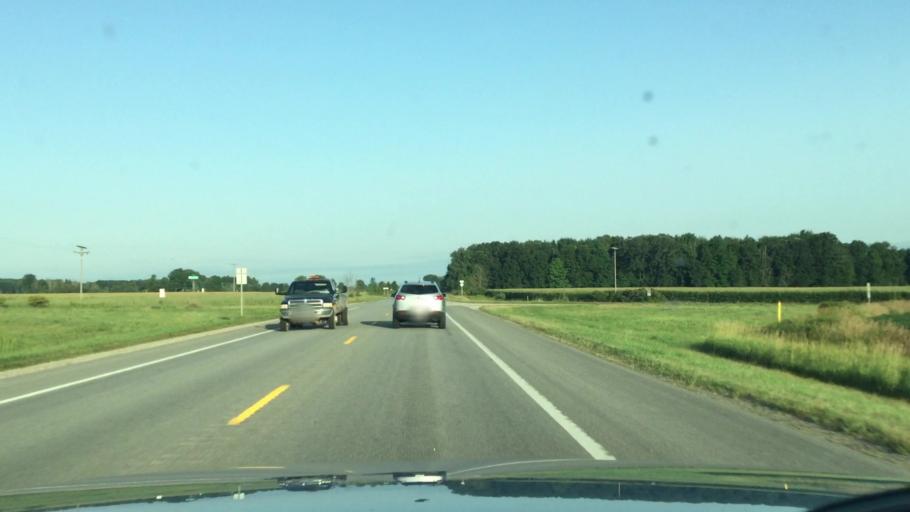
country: US
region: Michigan
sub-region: Montcalm County
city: Carson City
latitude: 43.1762
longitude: -84.7275
